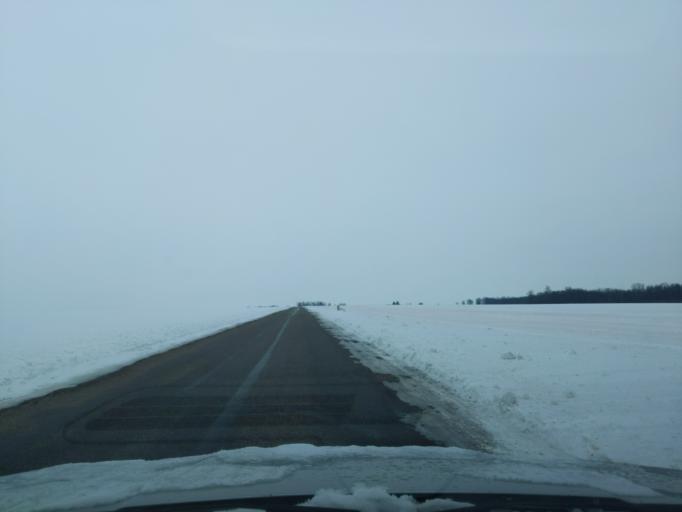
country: US
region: Indiana
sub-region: Benton County
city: Otterbein
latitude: 40.4288
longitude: -87.0928
